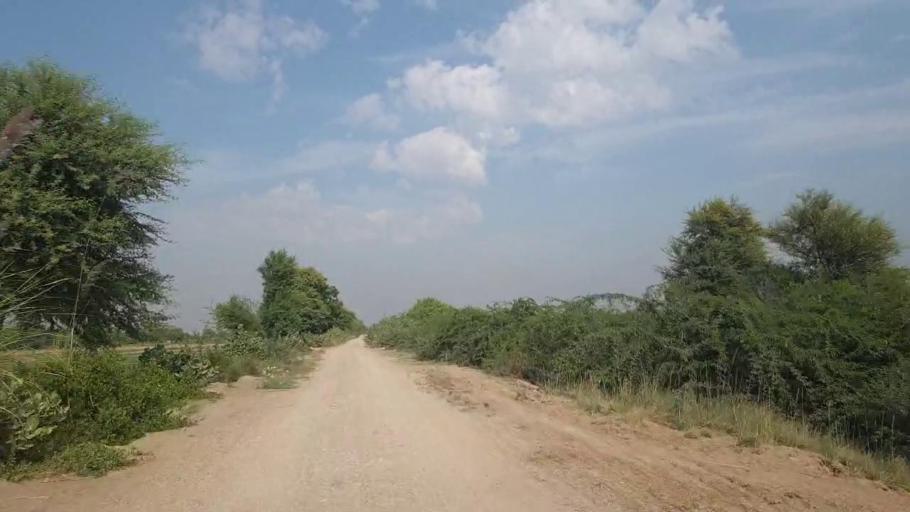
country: PK
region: Sindh
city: Digri
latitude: 25.0173
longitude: 69.0678
